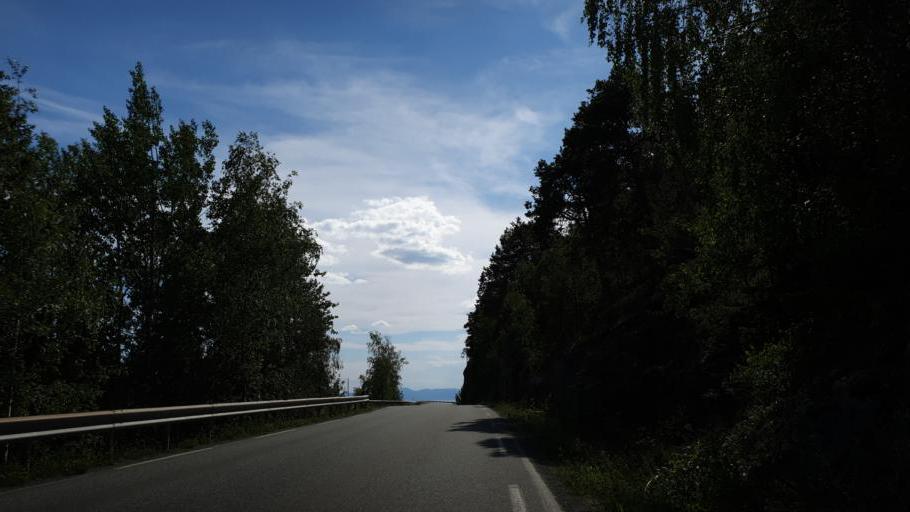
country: NO
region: Nord-Trondelag
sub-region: Leksvik
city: Leksvik
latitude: 63.6303
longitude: 10.5679
